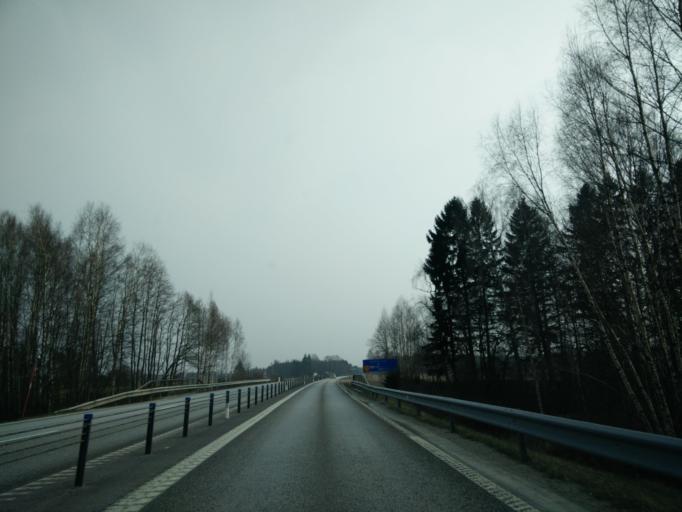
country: SE
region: Vaermland
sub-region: Forshaga Kommun
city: Forshaga
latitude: 59.4632
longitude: 13.4160
